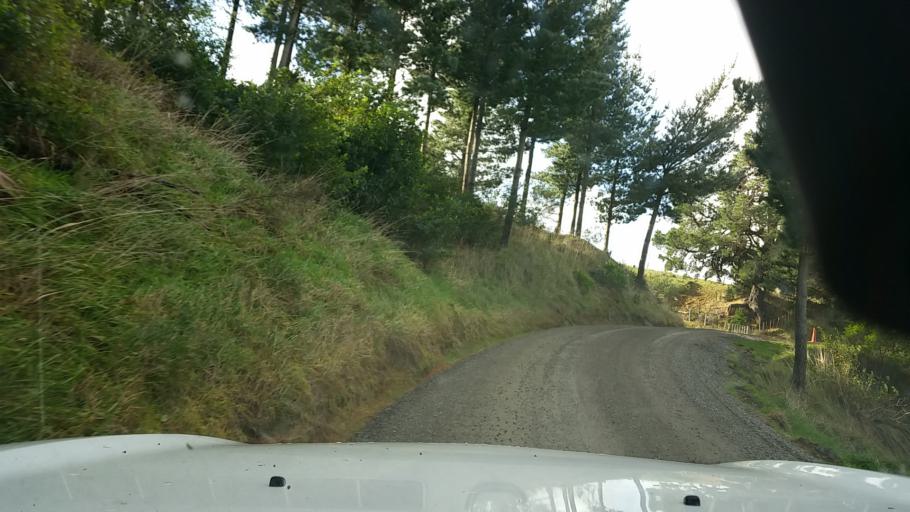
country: NZ
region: Wellington
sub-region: Masterton District
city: Masterton
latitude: -41.1855
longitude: 175.9640
